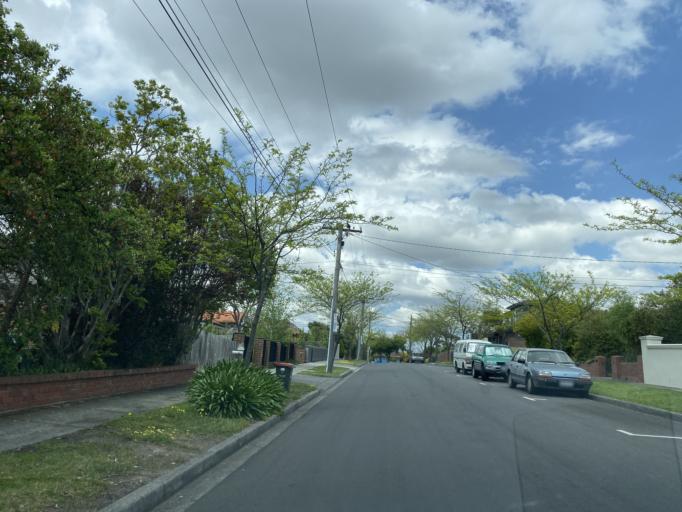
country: AU
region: Victoria
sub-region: Monash
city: Ashwood
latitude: -37.8526
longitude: 145.0977
